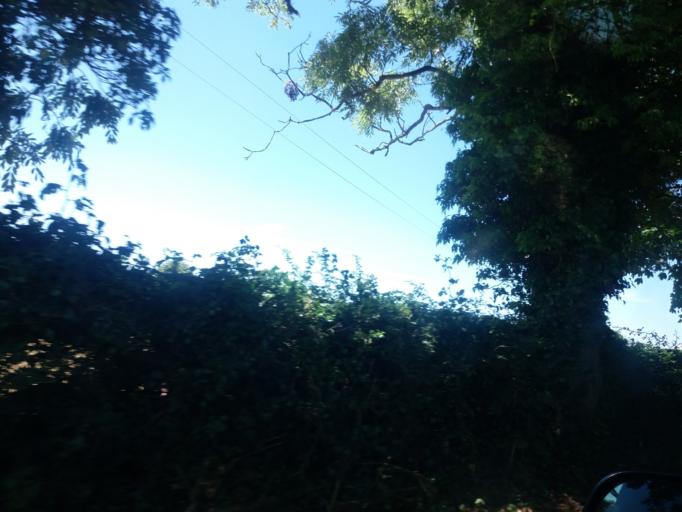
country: IE
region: Leinster
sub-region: Dublin City
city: Finglas
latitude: 53.4384
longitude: -6.3076
